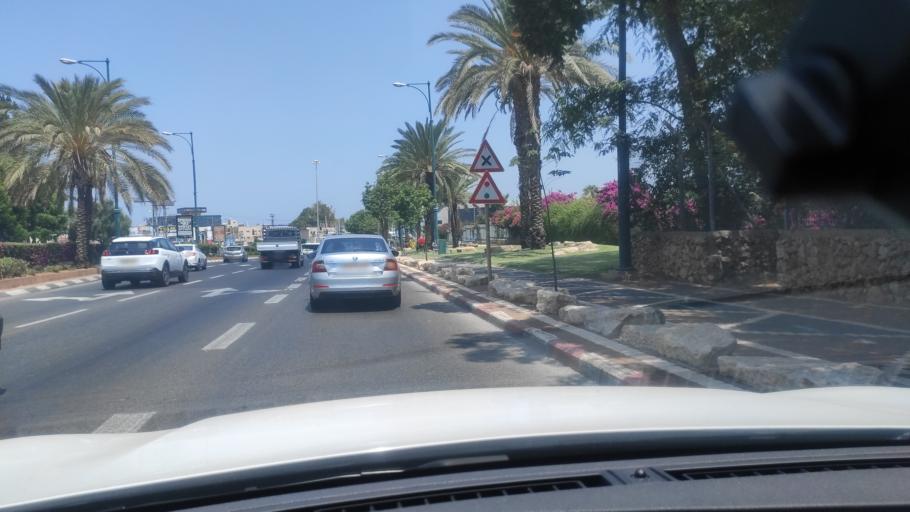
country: IL
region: Central District
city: Petah Tiqwa
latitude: 32.1006
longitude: 34.8990
